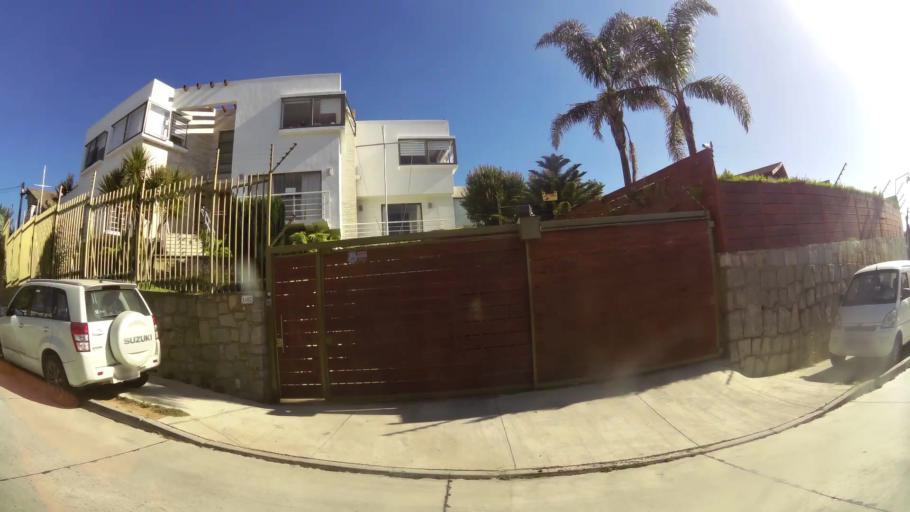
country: CL
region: Valparaiso
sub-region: Provincia de Valparaiso
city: Vina del Mar
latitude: -33.0353
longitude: -71.5578
